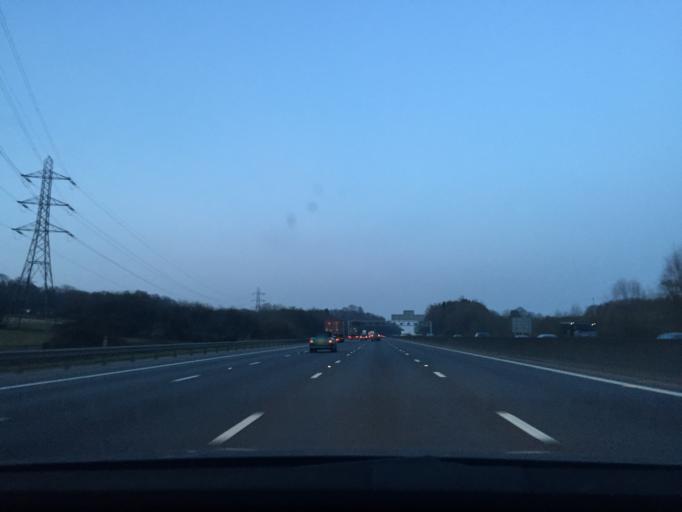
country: GB
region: England
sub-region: Hampshire
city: Totton
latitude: 50.9520
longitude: -1.4624
